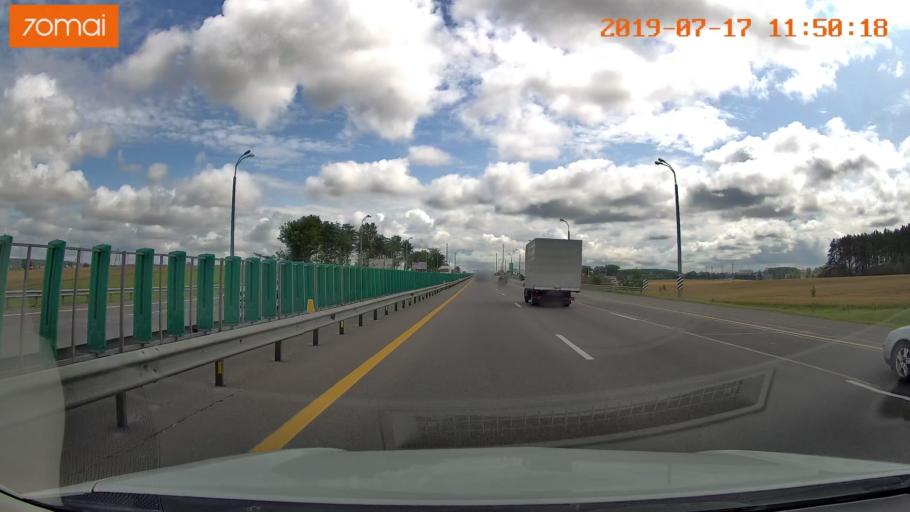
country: BY
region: Minsk
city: Bal'shavik
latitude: 53.9685
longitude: 27.5198
